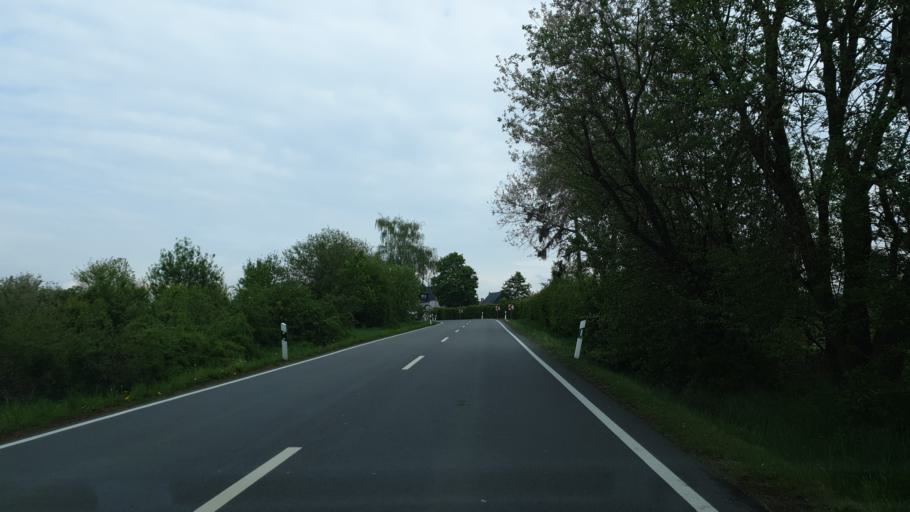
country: DE
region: Saxony
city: Gersdorf
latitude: 50.7527
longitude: 12.7214
